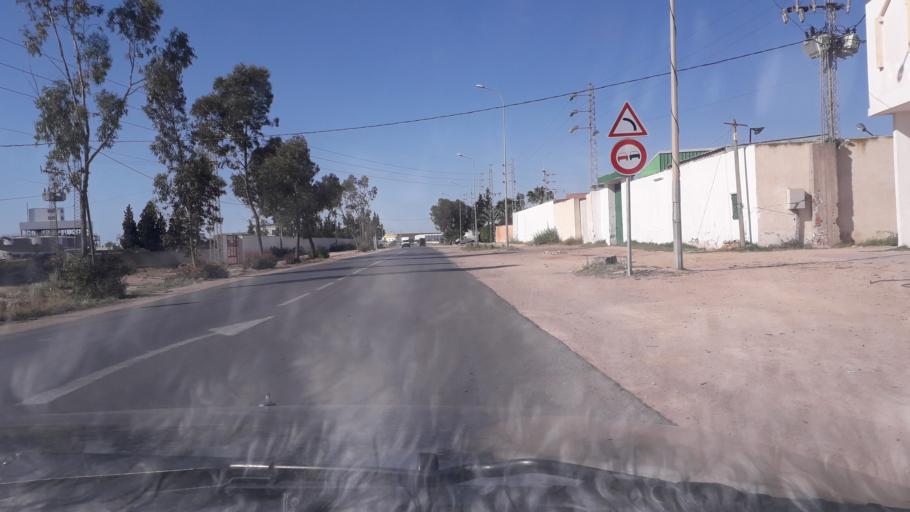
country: TN
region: Safaqis
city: Al Qarmadah
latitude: 34.8800
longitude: 10.7588
